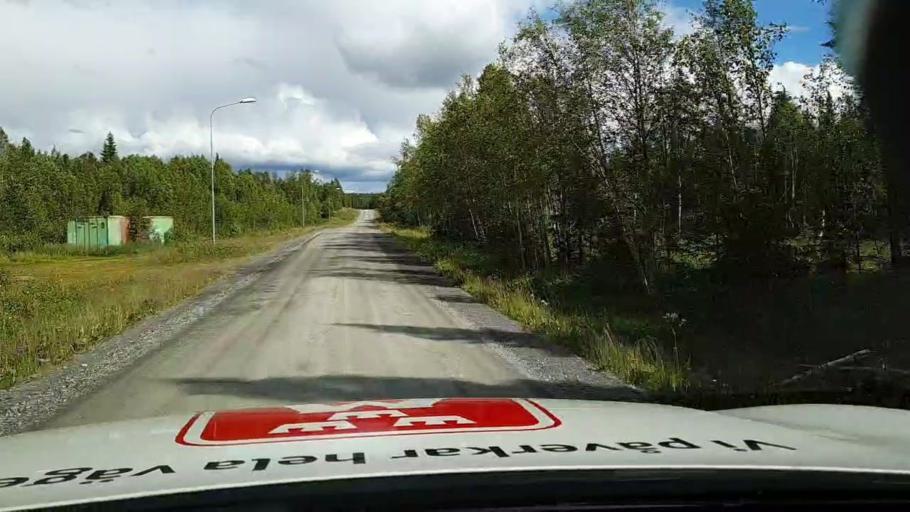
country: SE
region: Jaemtland
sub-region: Krokoms Kommun
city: Valla
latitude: 63.6943
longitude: 13.6535
